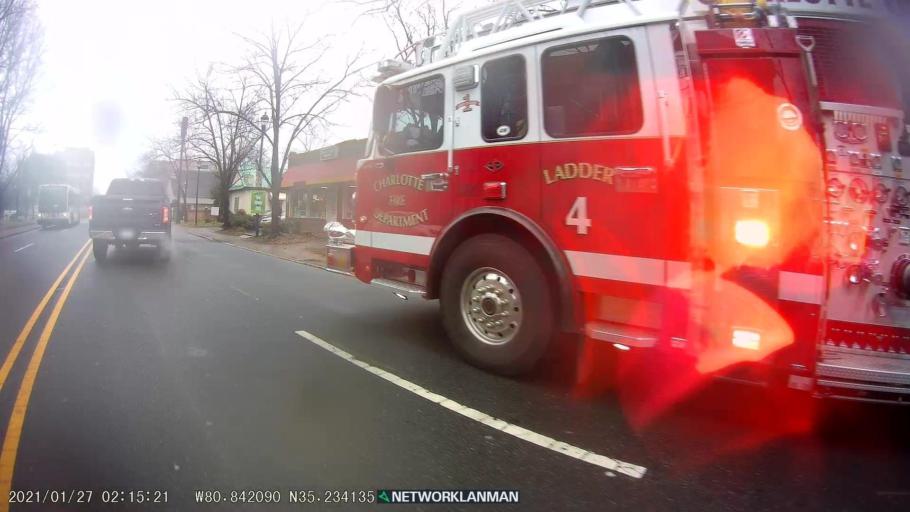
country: US
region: North Carolina
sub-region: Mecklenburg County
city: Charlotte
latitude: 35.2342
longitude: -80.8422
